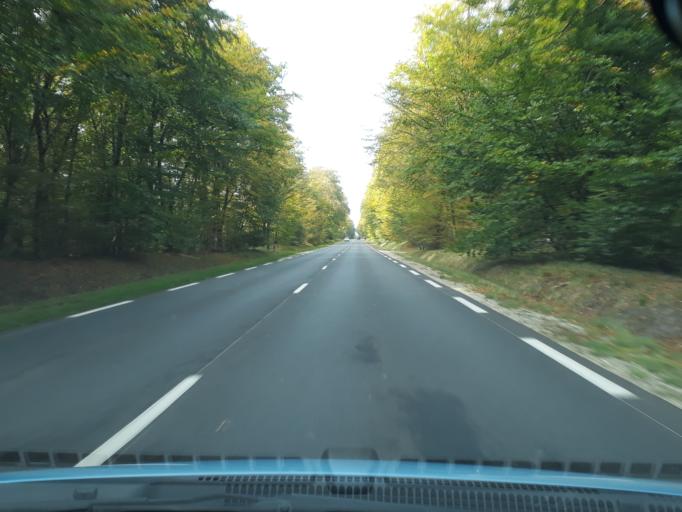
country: FR
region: Ile-de-France
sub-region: Departement de Seine-et-Marne
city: Bourron-Marlotte
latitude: 48.3692
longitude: 2.6384
